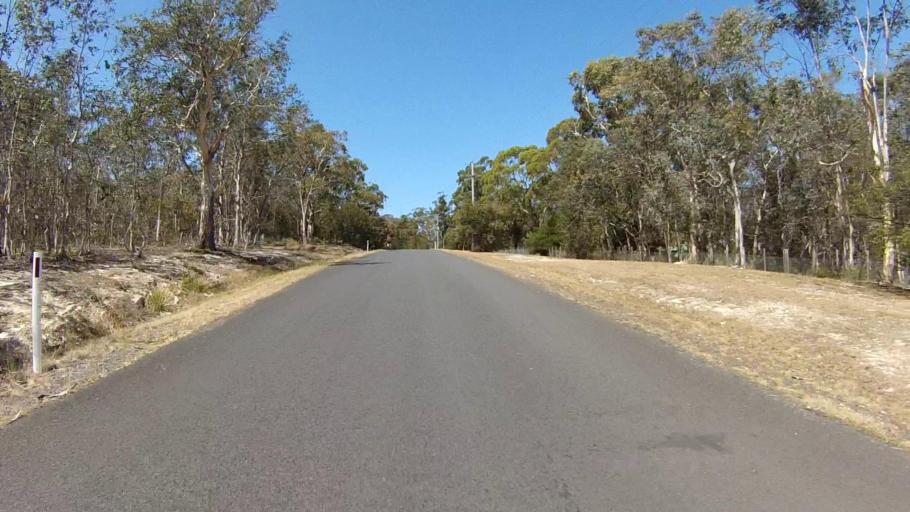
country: AU
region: Tasmania
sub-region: Clarence
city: Sandford
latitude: -42.9754
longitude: 147.4805
